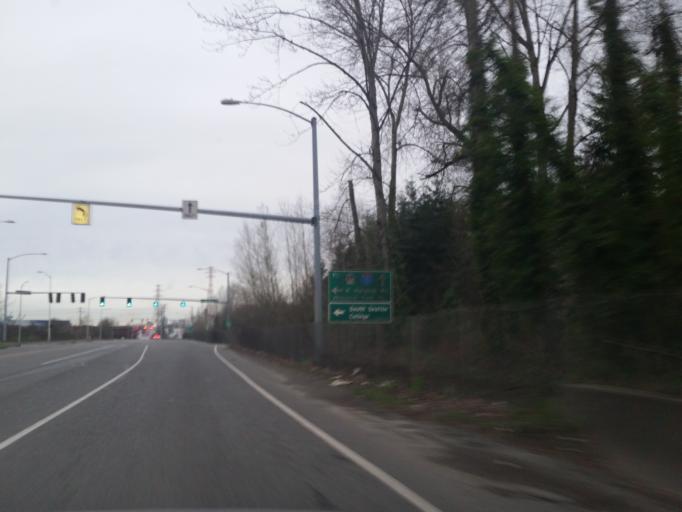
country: US
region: Washington
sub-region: King County
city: White Center
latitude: 47.5365
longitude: -122.3371
